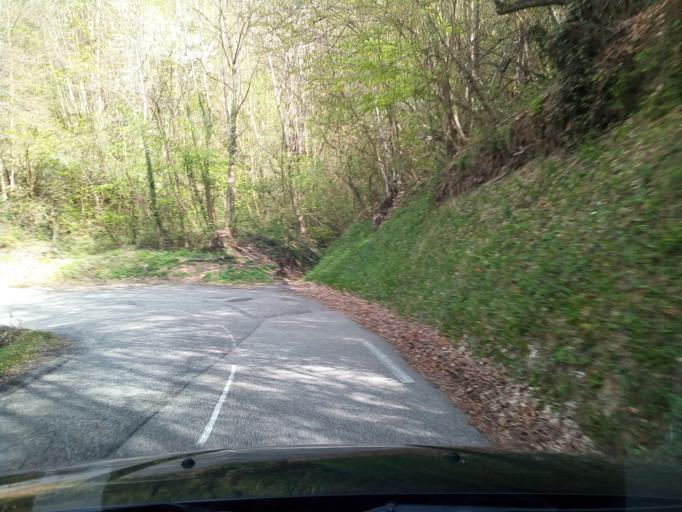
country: FR
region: Rhone-Alpes
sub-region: Departement de l'Isere
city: Gieres
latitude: 45.1640
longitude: 5.8137
